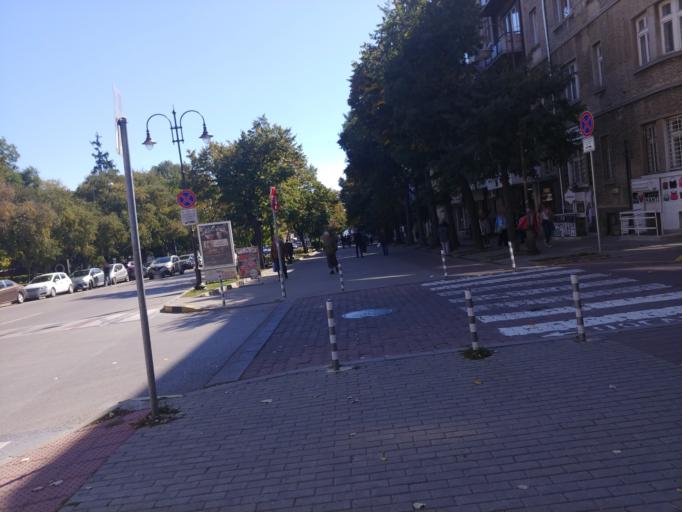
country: BG
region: Varna
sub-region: Obshtina Varna
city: Varna
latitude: 43.2068
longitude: 27.9179
